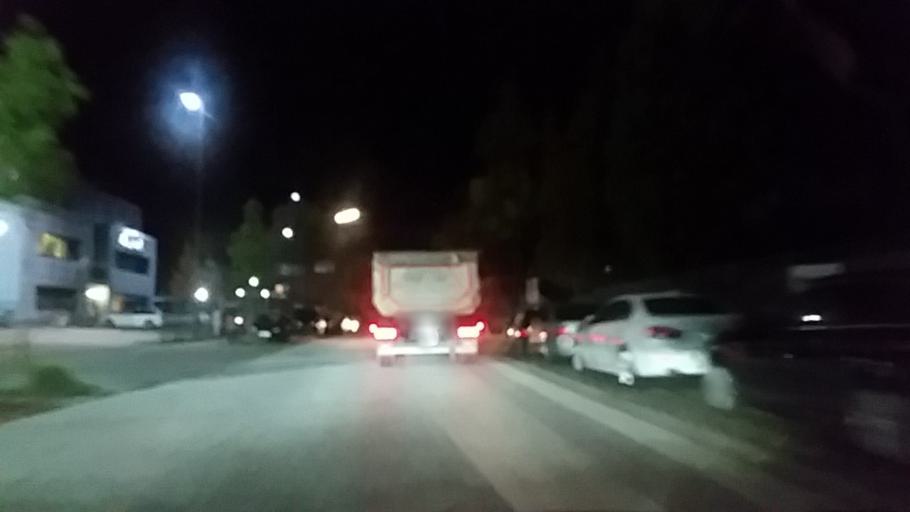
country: DE
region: Hamburg
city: Wandsbek
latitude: 53.5363
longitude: 10.0965
